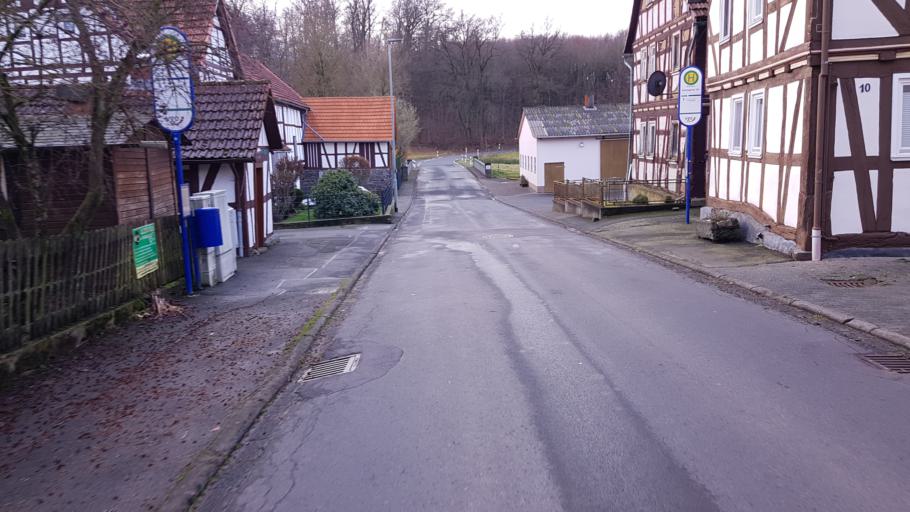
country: DE
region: Hesse
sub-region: Regierungsbezirk Giessen
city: Grunberg
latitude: 50.6316
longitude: 9.0478
